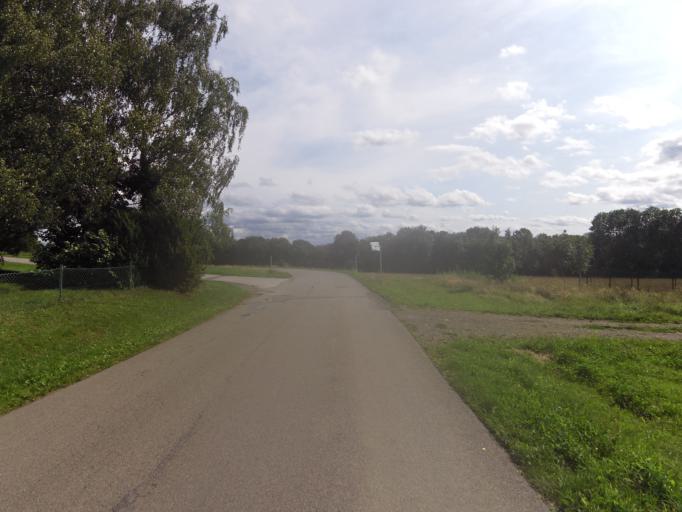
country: BE
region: Wallonia
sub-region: Province du Luxembourg
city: Durbuy
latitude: 50.3467
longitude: 5.4617
